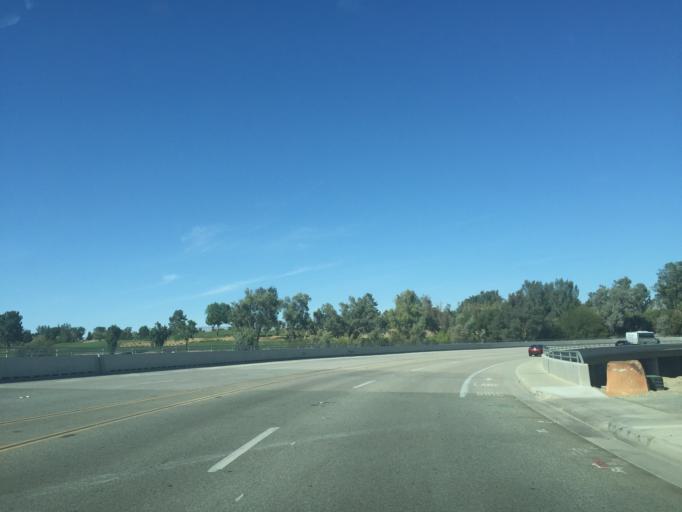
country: US
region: California
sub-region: Riverside County
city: Indian Wells
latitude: 33.7219
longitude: -116.3175
